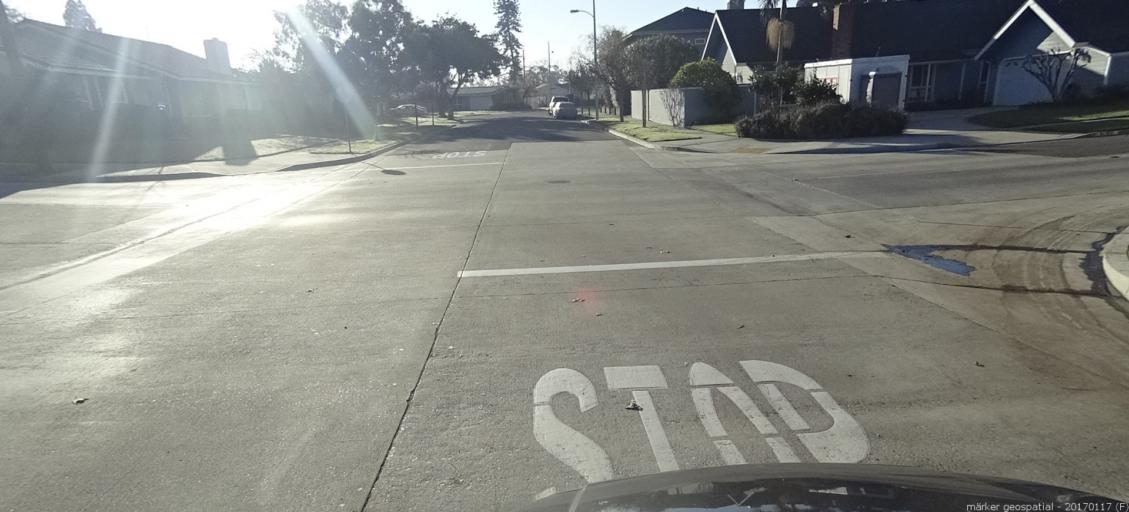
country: US
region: California
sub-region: Orange County
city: Rossmoor
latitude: 33.7790
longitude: -118.0797
